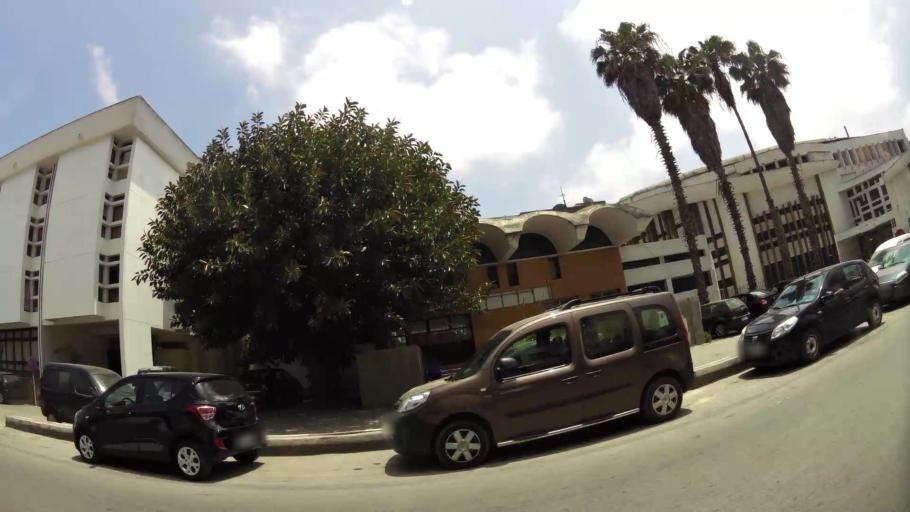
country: MA
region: Rabat-Sale-Zemmour-Zaer
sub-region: Rabat
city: Rabat
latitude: 34.0058
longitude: -6.8464
